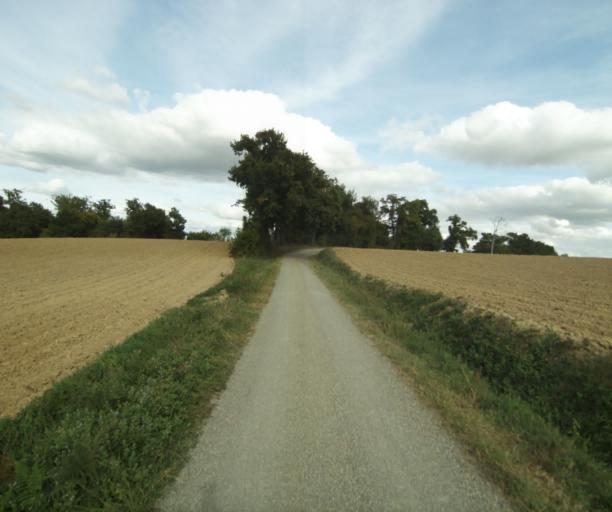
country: FR
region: Midi-Pyrenees
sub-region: Departement du Gers
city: Eauze
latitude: 43.8344
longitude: 0.1717
